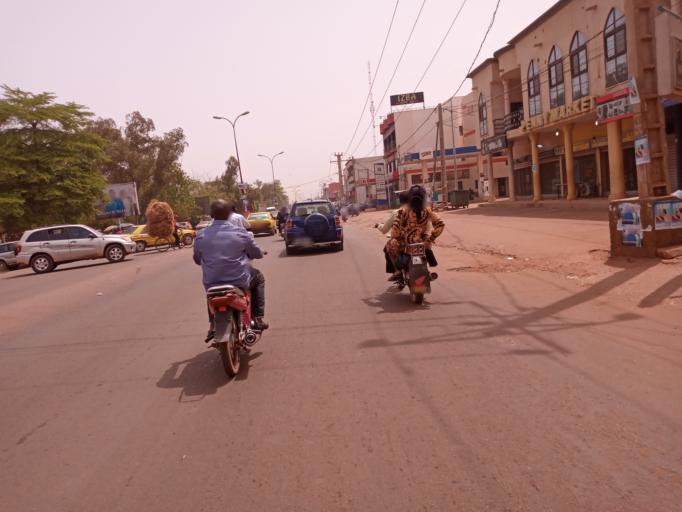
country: ML
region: Bamako
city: Bamako
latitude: 12.6648
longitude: -7.9383
